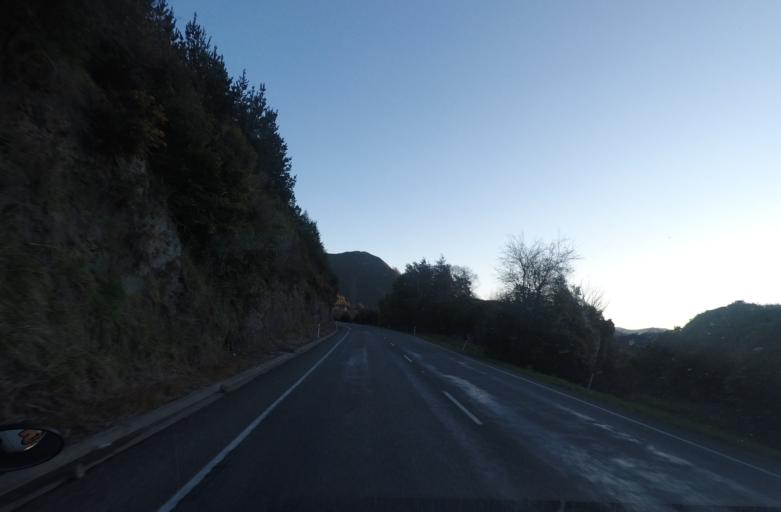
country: NZ
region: Marlborough
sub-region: Marlborough District
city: Picton
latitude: -41.2848
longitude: 173.7120
